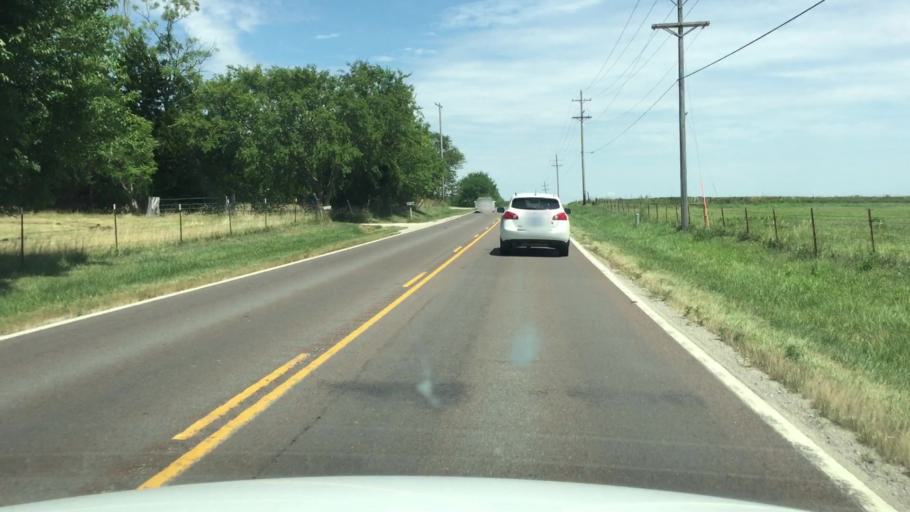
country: US
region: Kansas
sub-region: Douglas County
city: Lawrence
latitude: 38.9714
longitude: -95.3714
